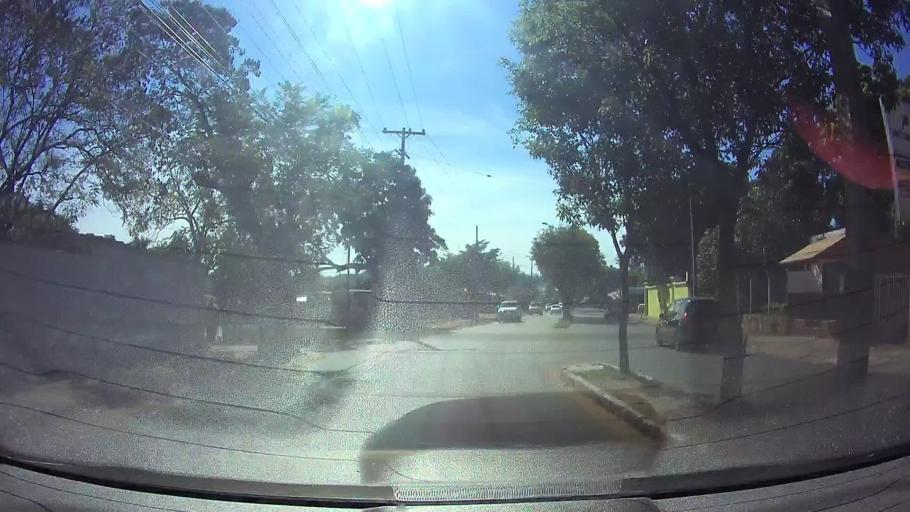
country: PY
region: Central
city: Villa Elisa
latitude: -25.3613
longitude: -57.5759
